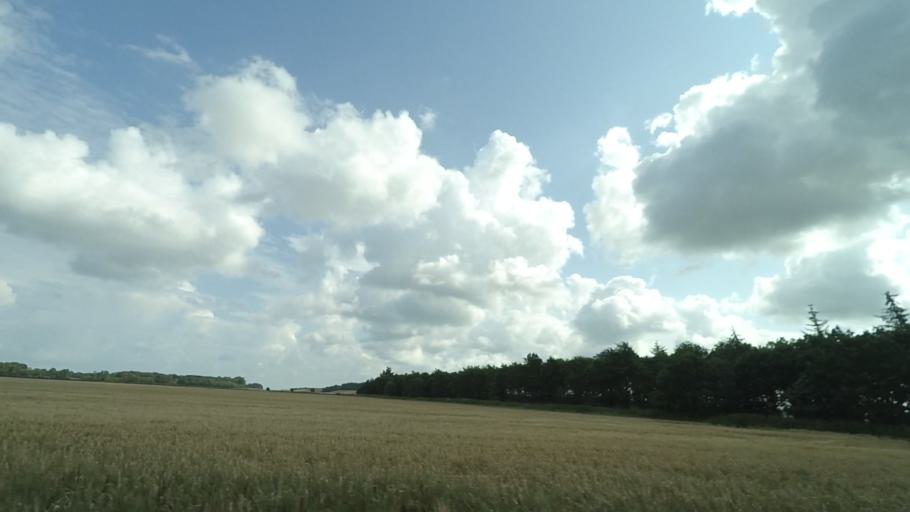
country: DK
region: Central Jutland
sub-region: Norddjurs Kommune
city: Auning
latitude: 56.5046
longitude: 10.4243
